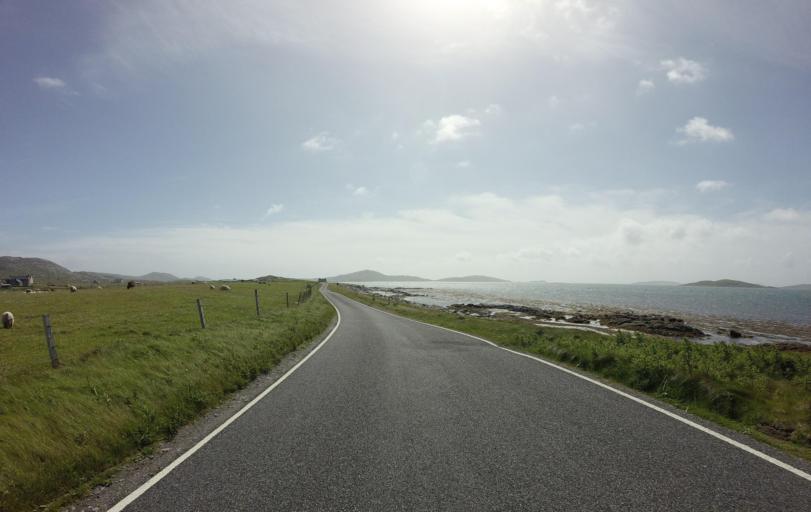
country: GB
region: Scotland
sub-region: Eilean Siar
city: Isle of South Uist
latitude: 57.1048
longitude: -7.3657
